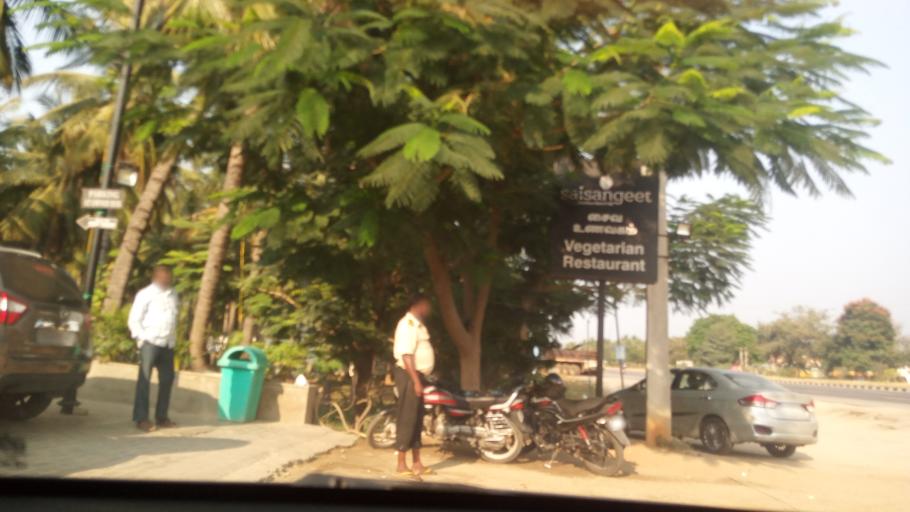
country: IN
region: Tamil Nadu
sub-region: Vellore
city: Vaniyambadi
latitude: 12.7194
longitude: 78.6625
